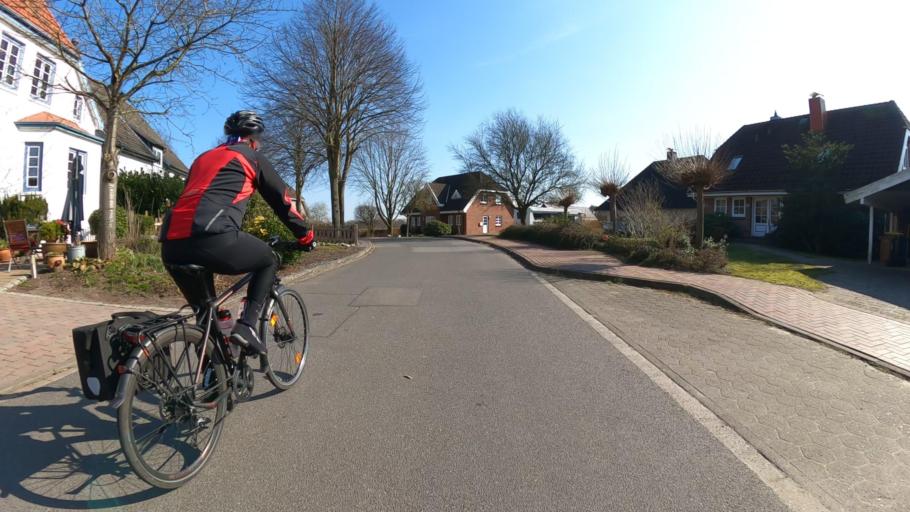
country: DE
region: Schleswig-Holstein
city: Seester
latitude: 53.7192
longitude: 9.5800
